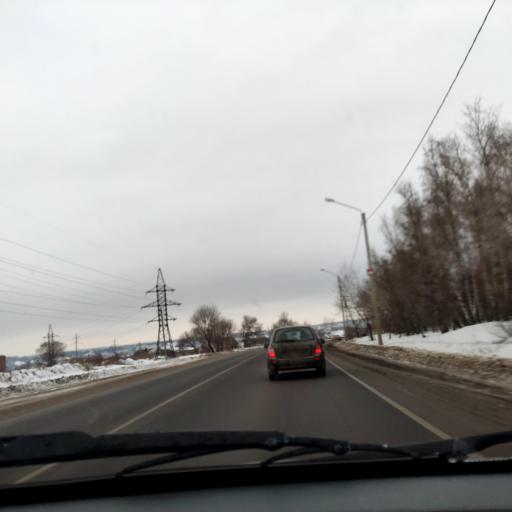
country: RU
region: Voronezj
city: Pridonskoy
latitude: 51.6987
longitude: 39.0821
